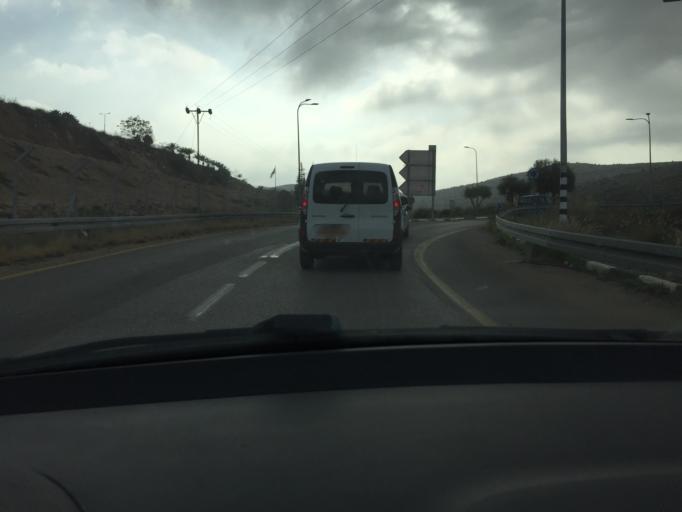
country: PS
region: West Bank
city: Al Lubban al Gharbi
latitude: 32.0336
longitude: 35.0481
